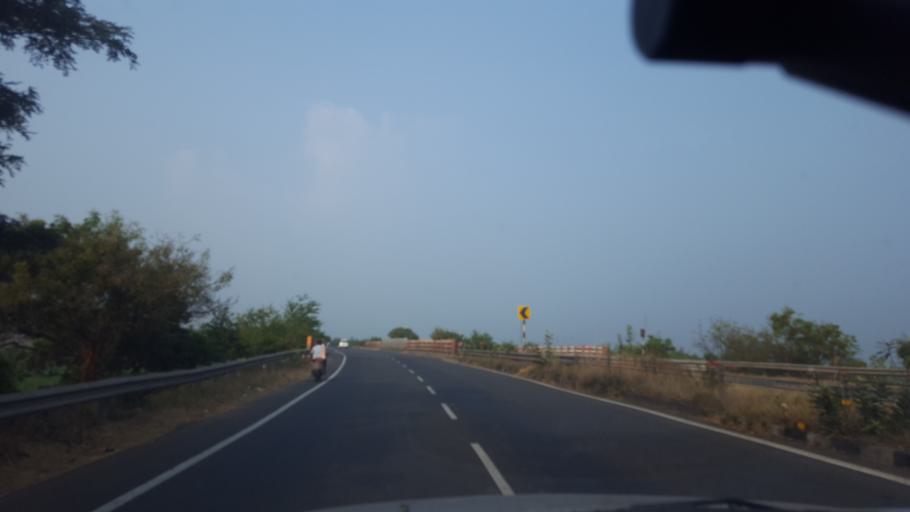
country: IN
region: Andhra Pradesh
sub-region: West Godavari
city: Tadepallegudem
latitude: 16.8267
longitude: 81.4661
